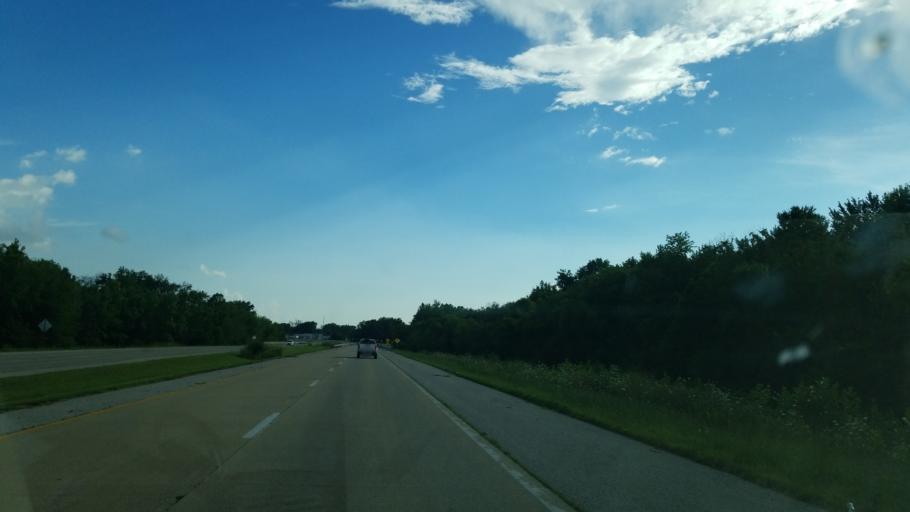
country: US
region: Illinois
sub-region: Marion County
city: Central City
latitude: 38.5582
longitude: -89.1250
